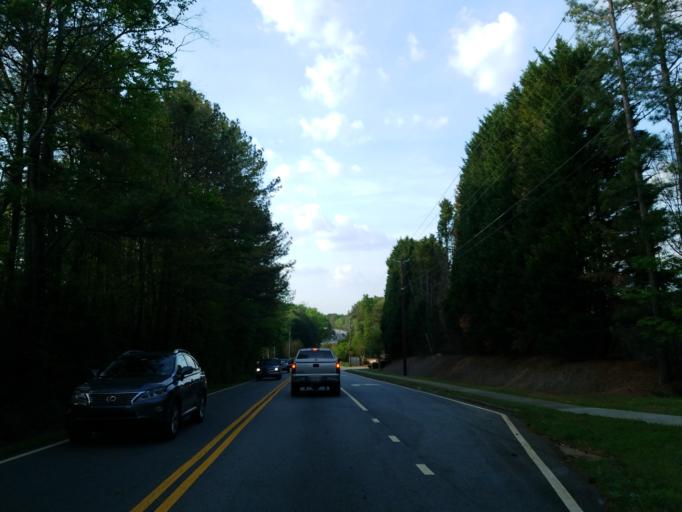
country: US
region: Georgia
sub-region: Fulton County
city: Roswell
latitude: 34.0662
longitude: -84.3609
